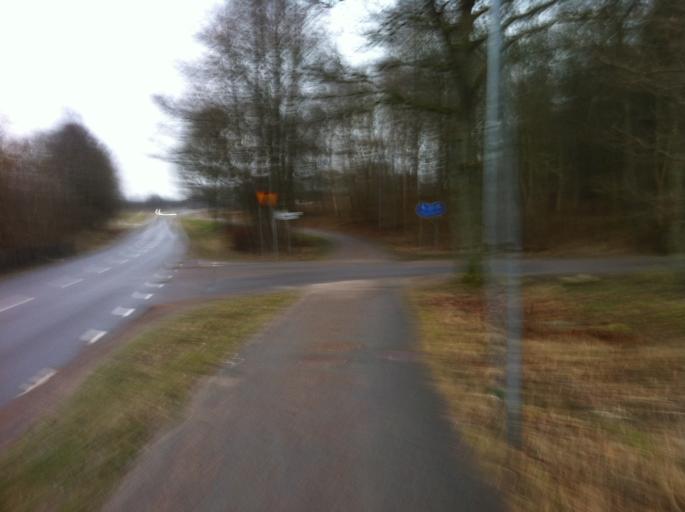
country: SE
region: Skane
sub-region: Hoors Kommun
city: Satofta
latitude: 55.9138
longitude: 13.5483
